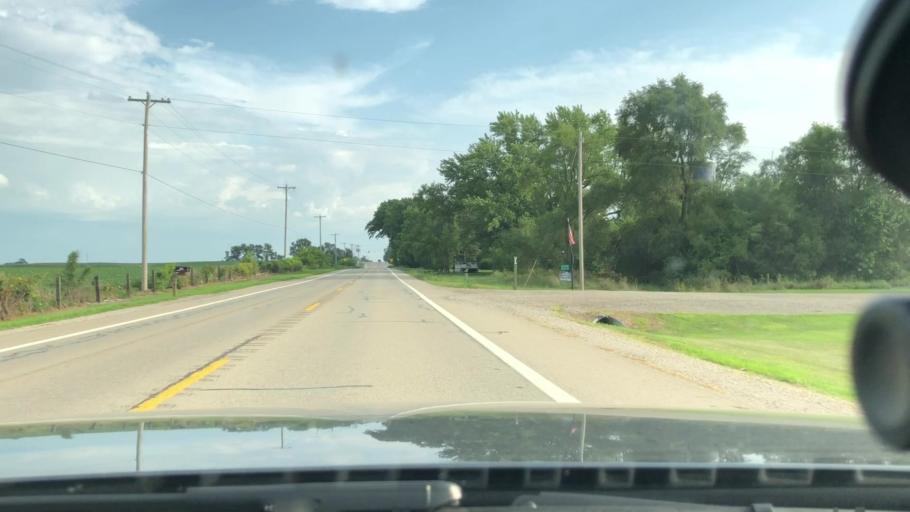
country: US
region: Michigan
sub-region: Washtenaw County
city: Manchester
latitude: 42.1967
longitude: -84.0326
